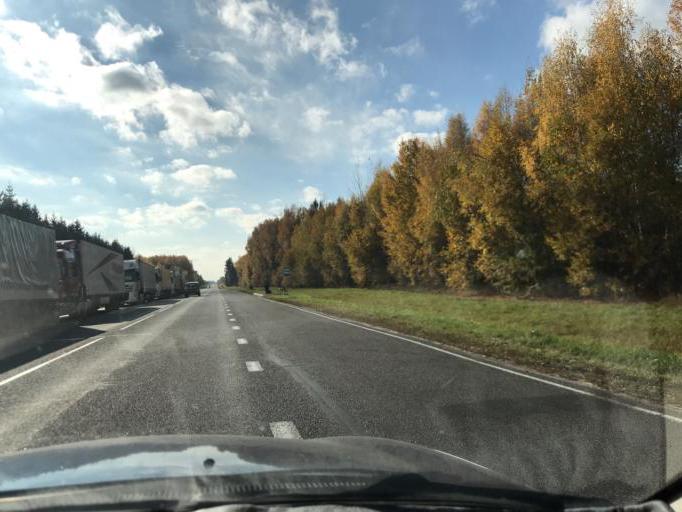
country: LT
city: Salcininkai
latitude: 54.2216
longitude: 25.3555
